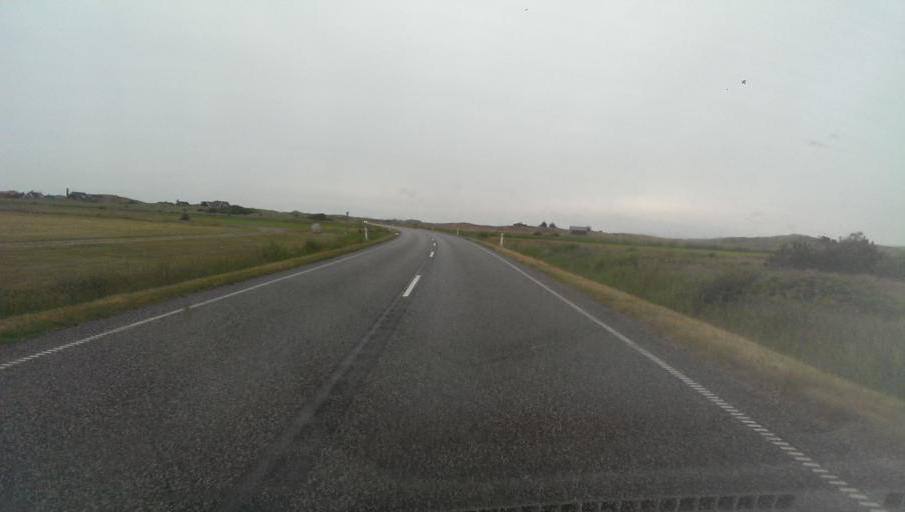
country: DK
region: Central Jutland
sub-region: Ringkobing-Skjern Kommune
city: Hvide Sande
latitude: 55.8846
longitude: 8.1761
